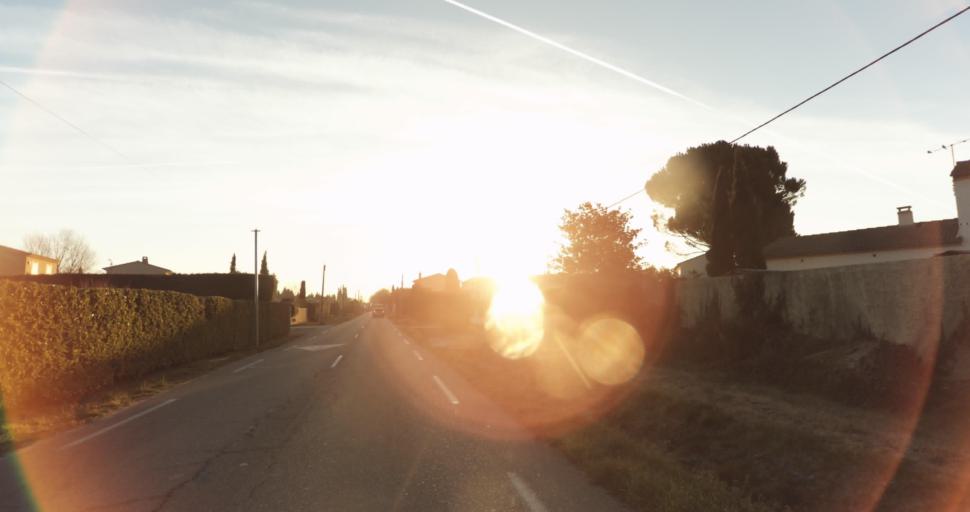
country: FR
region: Provence-Alpes-Cote d'Azur
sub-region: Departement des Bouches-du-Rhone
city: Barbentane
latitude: 43.8983
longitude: 4.7671
